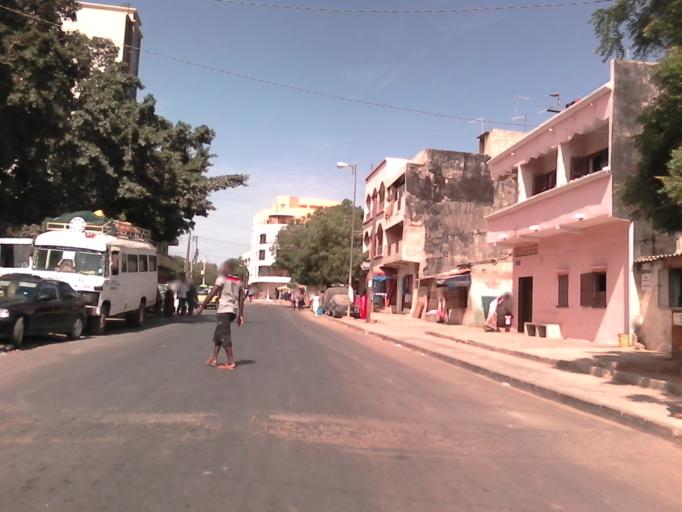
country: SN
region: Dakar
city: Grand Dakar
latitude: 14.7062
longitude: -17.4580
